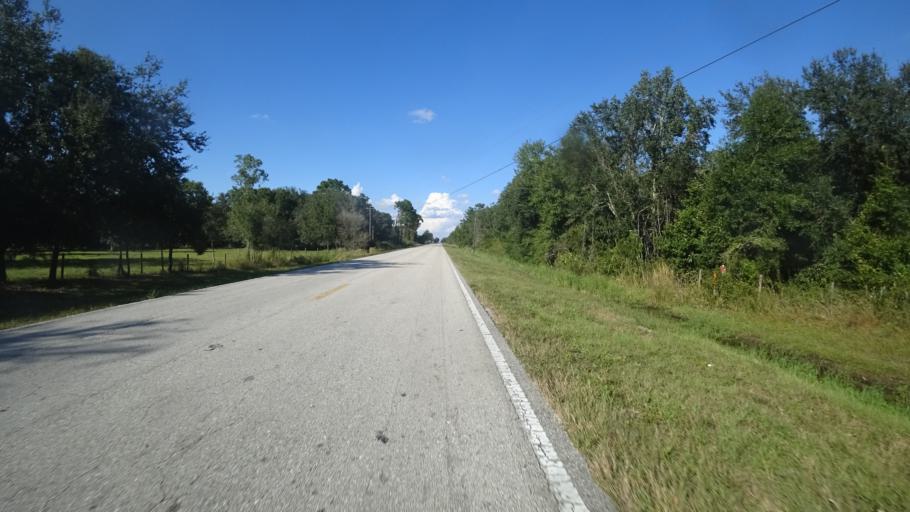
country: US
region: Florida
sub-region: Sarasota County
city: The Meadows
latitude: 27.4372
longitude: -82.3035
